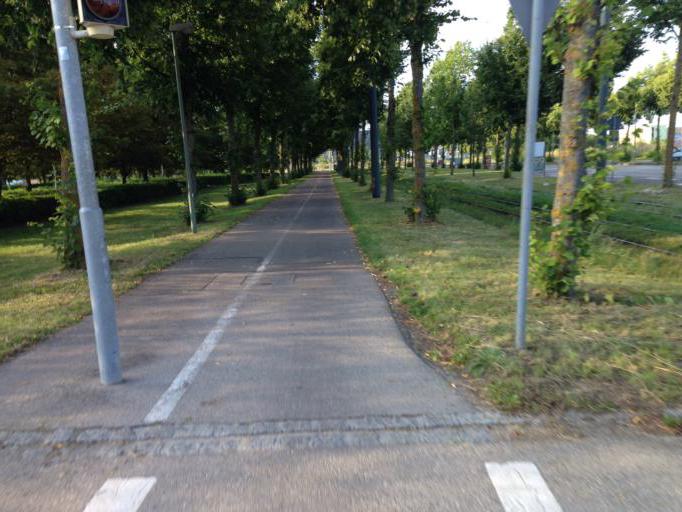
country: DE
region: Bavaria
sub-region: Swabia
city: Augsburg
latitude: 48.3236
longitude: 10.8964
